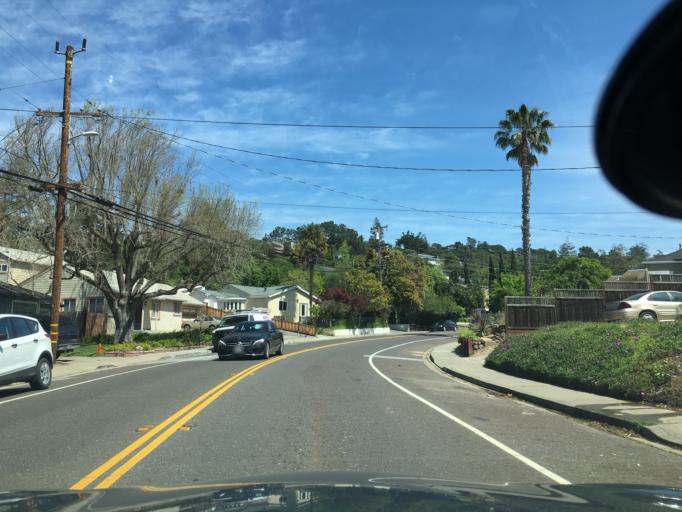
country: US
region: California
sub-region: San Mateo County
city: Belmont
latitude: 37.5075
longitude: -122.2844
